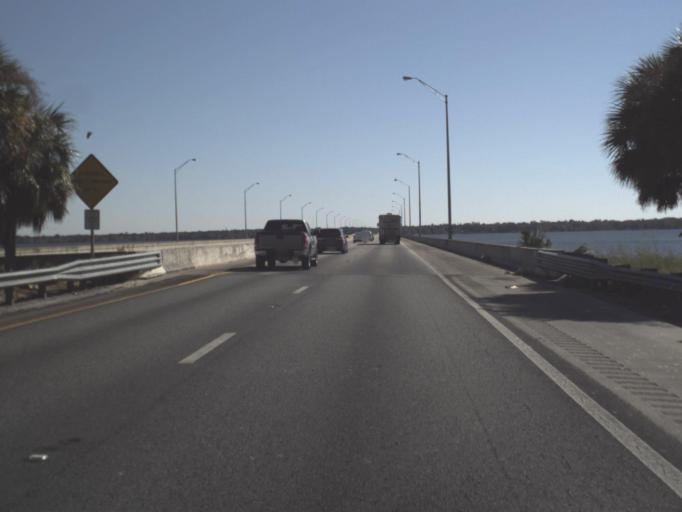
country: US
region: Florida
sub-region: Seminole County
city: Oviedo
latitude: 28.7210
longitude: -81.2442
